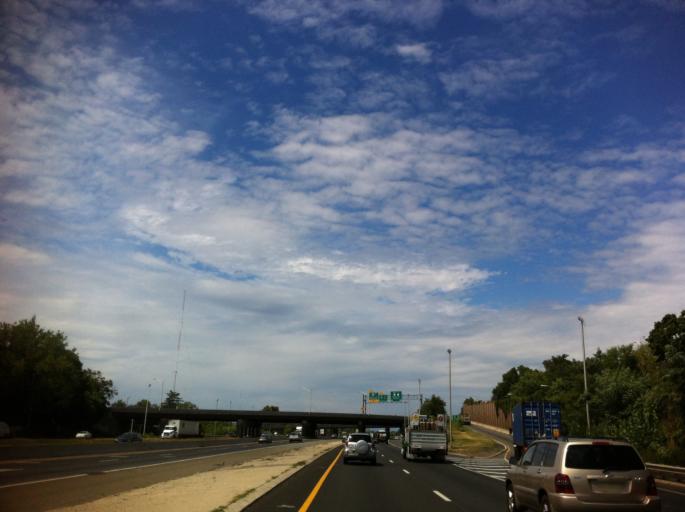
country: US
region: New Jersey
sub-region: Bergen County
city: Hackensack
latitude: 40.8696
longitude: -74.0563
